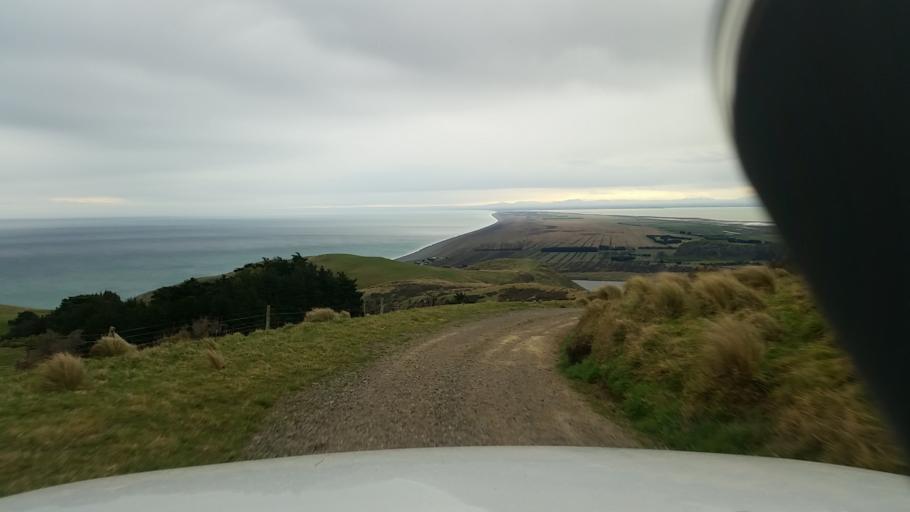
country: NZ
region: Canterbury
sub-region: Christchurch City
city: Christchurch
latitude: -43.8173
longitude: 172.7482
